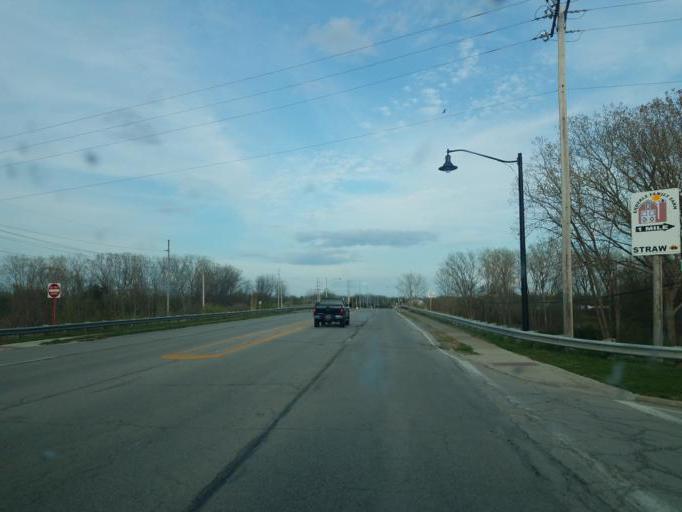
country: US
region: Ohio
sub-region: Erie County
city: Huron
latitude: 41.3897
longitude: -82.5528
